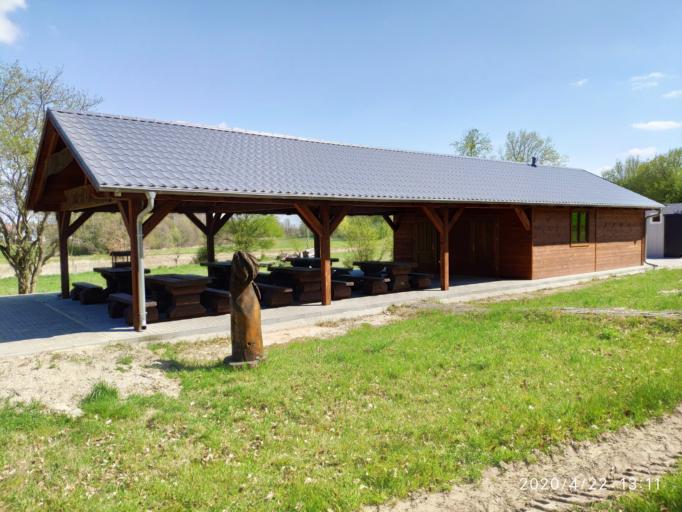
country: PL
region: Lubusz
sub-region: Powiat zielonogorski
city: Sulechow
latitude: 52.1116
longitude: 15.6986
